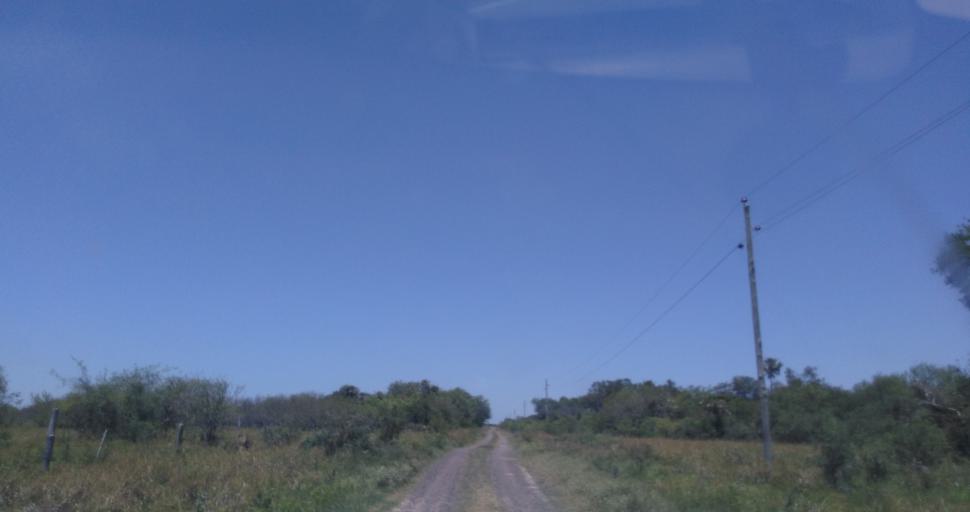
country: AR
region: Chaco
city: Fontana
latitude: -27.4792
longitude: -59.0696
